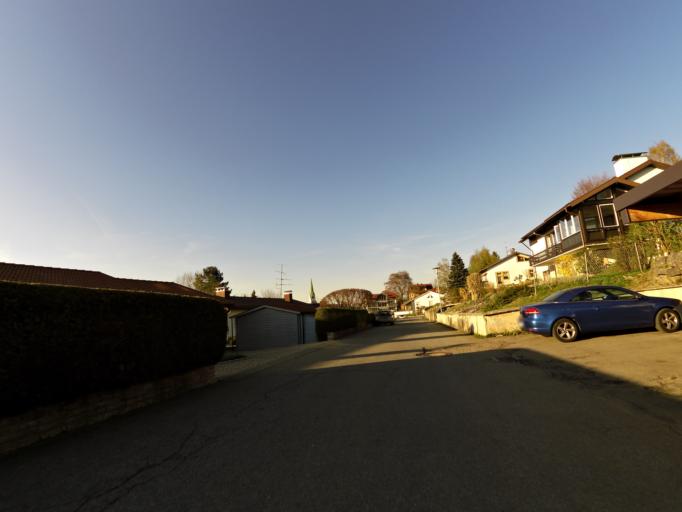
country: DE
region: Bavaria
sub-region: Swabia
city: Weiler-Simmerberg
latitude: 47.5783
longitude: 9.9150
